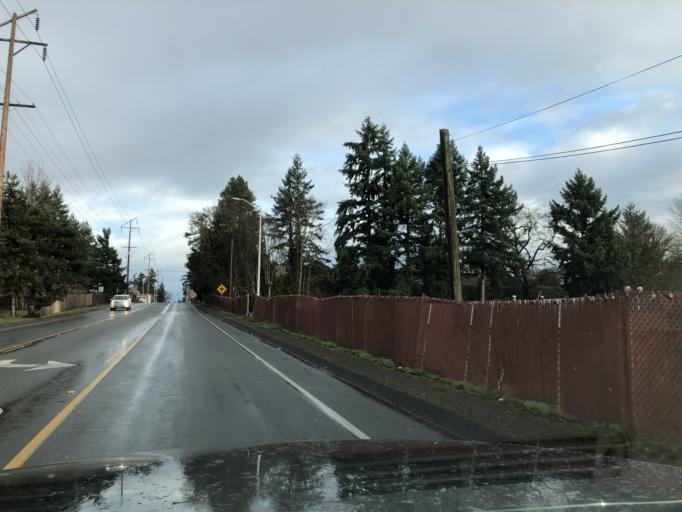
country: US
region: Washington
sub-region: Pierce County
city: Parkland
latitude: 47.1436
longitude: -122.4371
